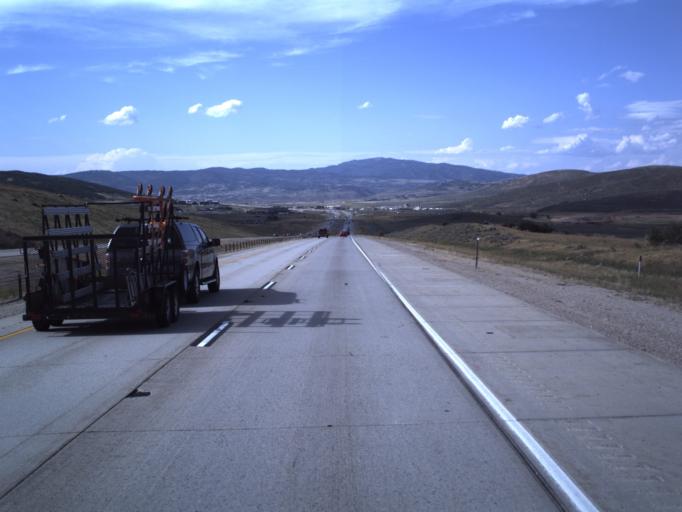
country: US
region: Utah
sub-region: Summit County
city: Park City
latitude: 40.6595
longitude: -111.4579
